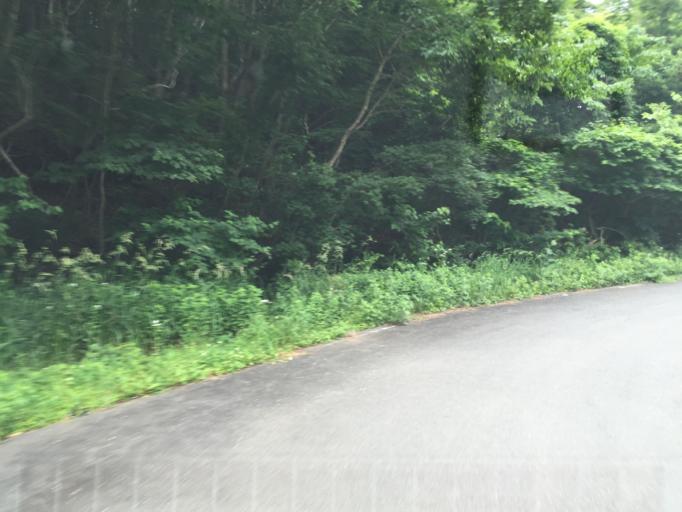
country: JP
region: Fukushima
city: Yanagawamachi-saiwaicho
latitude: 37.7951
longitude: 140.7069
